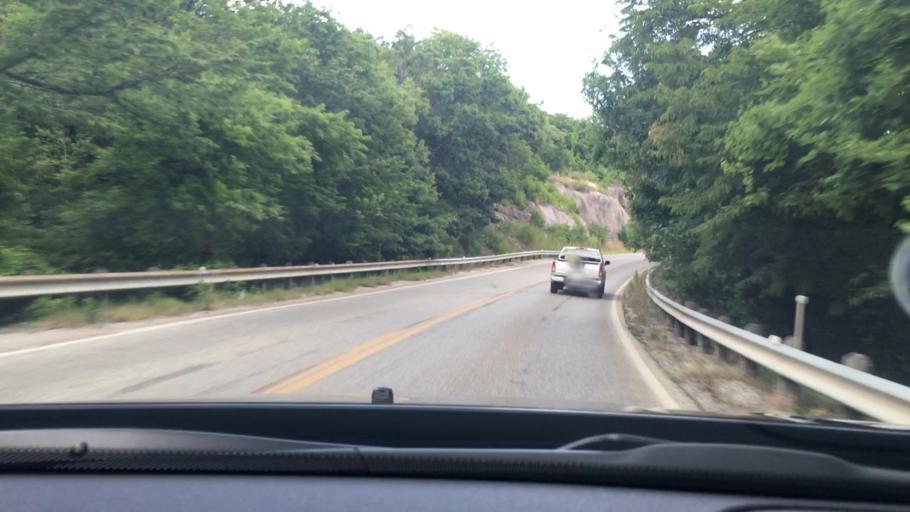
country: US
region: Oklahoma
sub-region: Pontotoc County
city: Ada
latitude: 34.5686
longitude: -96.6326
